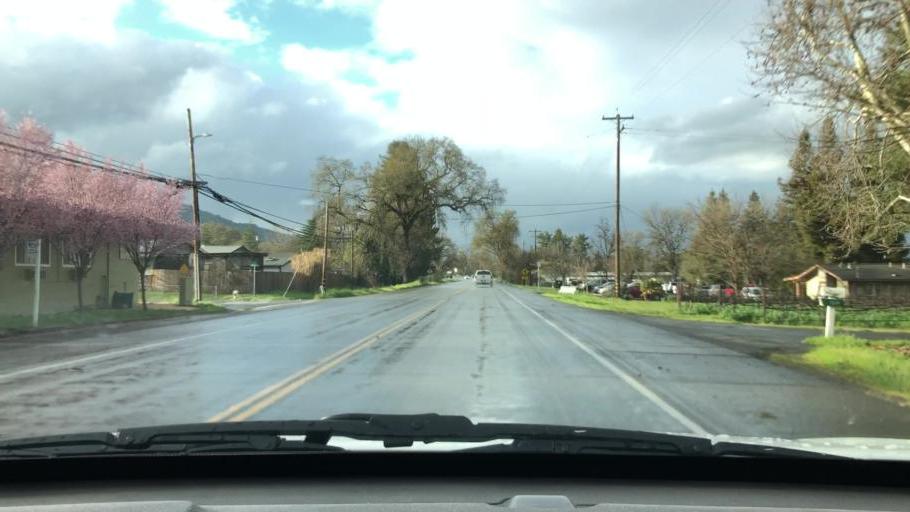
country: US
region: California
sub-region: Mendocino County
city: Talmage
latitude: 39.1142
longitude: -123.1988
